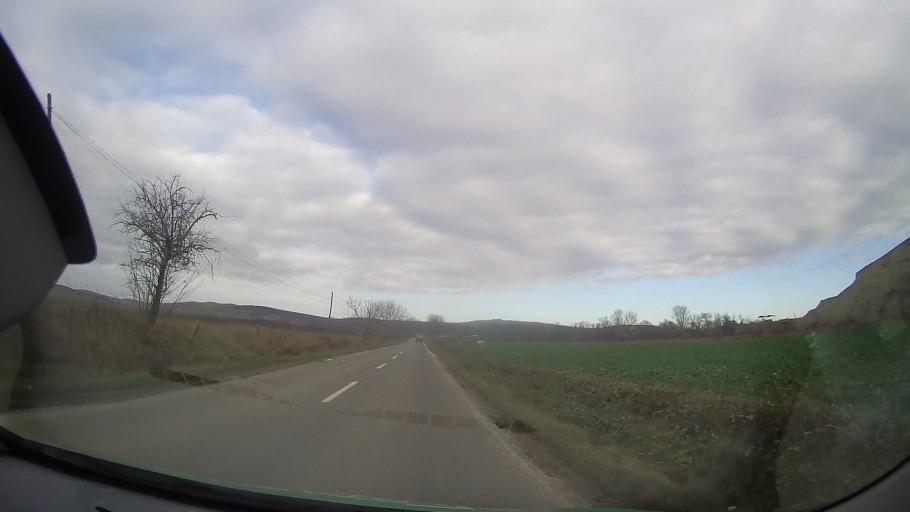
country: RO
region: Mures
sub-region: Comuna Iernut
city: Iernut
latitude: 46.4663
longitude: 24.2183
